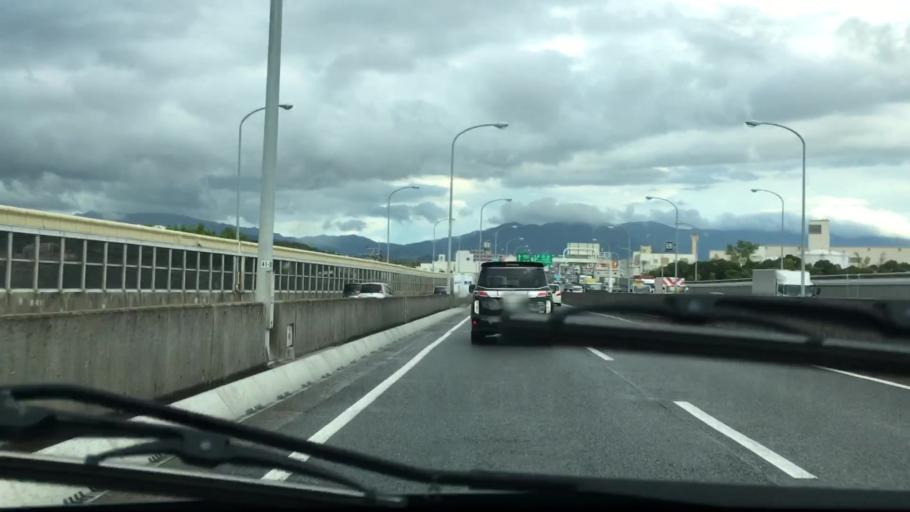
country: JP
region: Fukuoka
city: Fukuoka-shi
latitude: 33.6338
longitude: 130.4274
